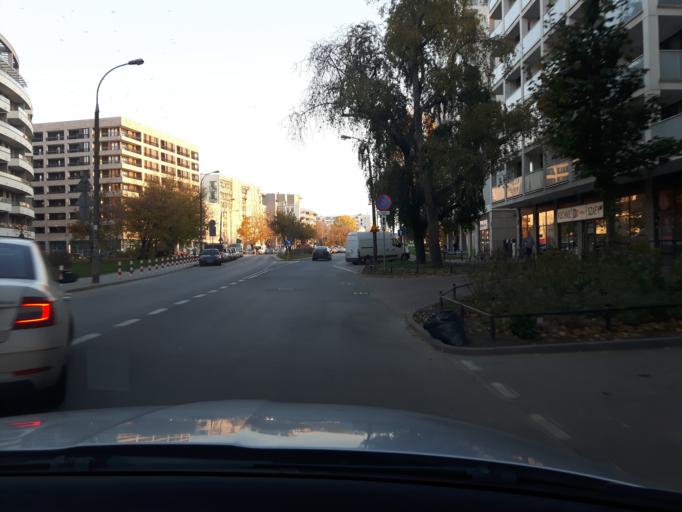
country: PL
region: Masovian Voivodeship
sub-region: Warszawa
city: Ochota
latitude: 52.2255
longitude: 20.9522
